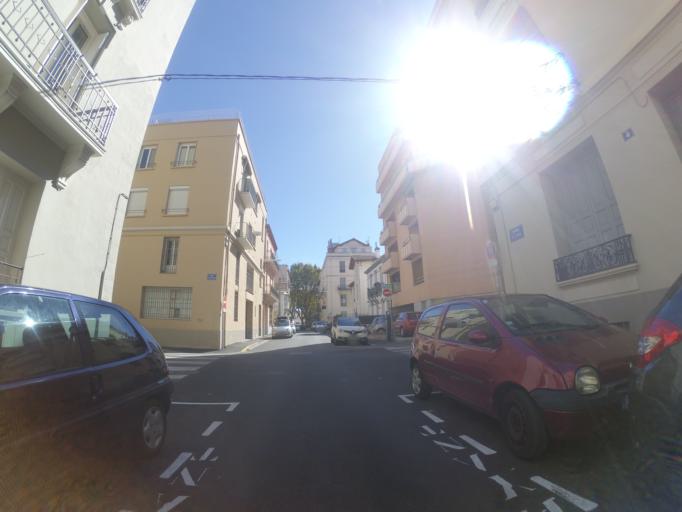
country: FR
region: Languedoc-Roussillon
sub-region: Departement des Pyrenees-Orientales
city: Perpignan
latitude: 42.6978
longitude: 2.8870
